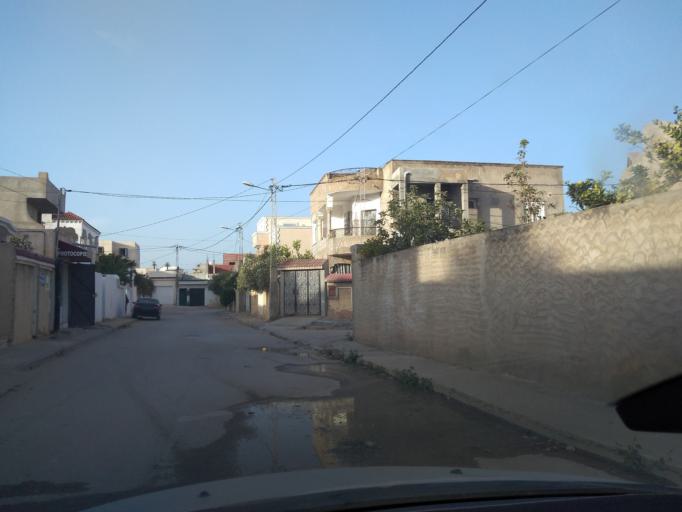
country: TN
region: Manouba
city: Manouba
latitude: 36.7926
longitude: 10.0865
